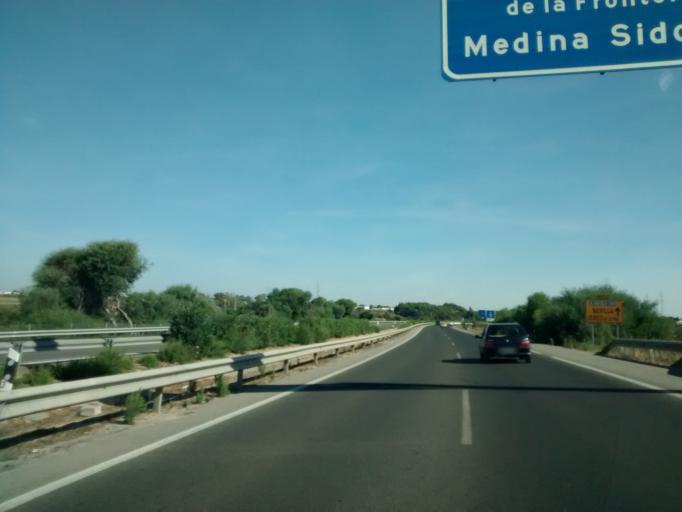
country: ES
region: Andalusia
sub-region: Provincia de Cadiz
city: Chiclana de la Frontera
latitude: 36.4118
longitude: -6.1188
